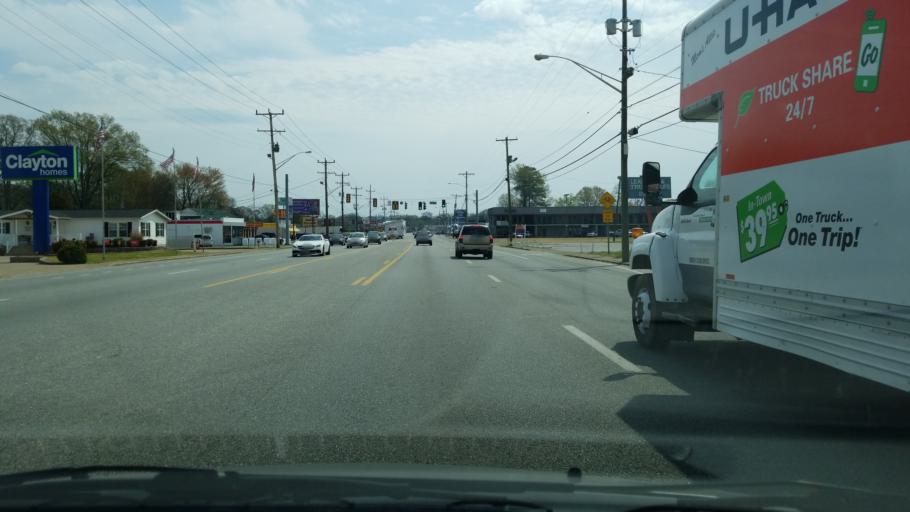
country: US
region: Tennessee
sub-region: Hamilton County
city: East Ridge
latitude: 34.9932
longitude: -85.2294
